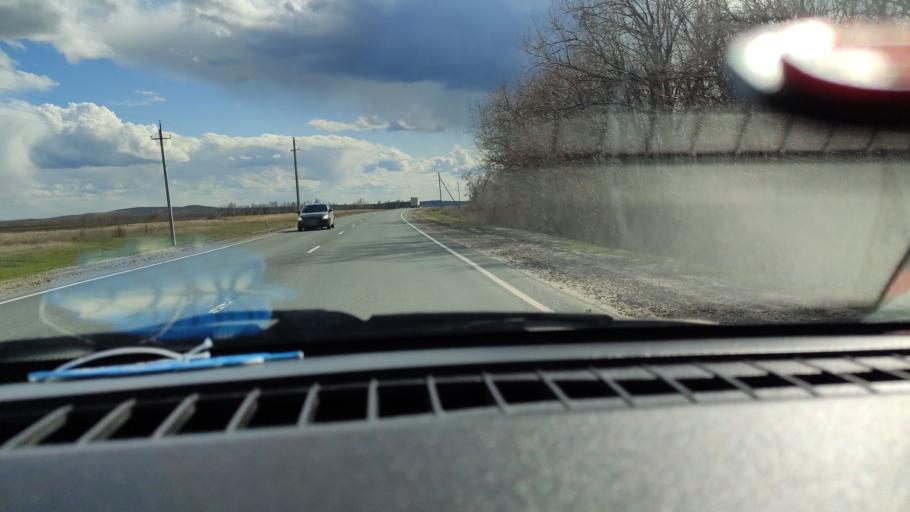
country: RU
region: Saratov
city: Alekseyevka
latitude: 52.2669
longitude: 47.9258
